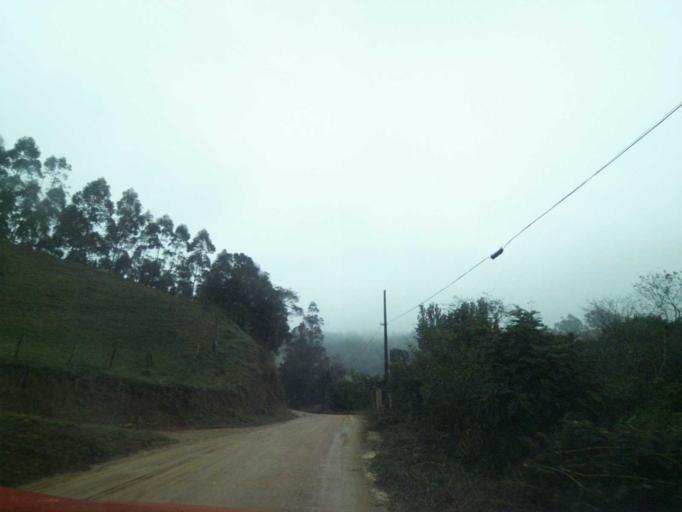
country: BR
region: Santa Catarina
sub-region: Anitapolis
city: Anitapolis
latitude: -27.9236
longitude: -49.1307
